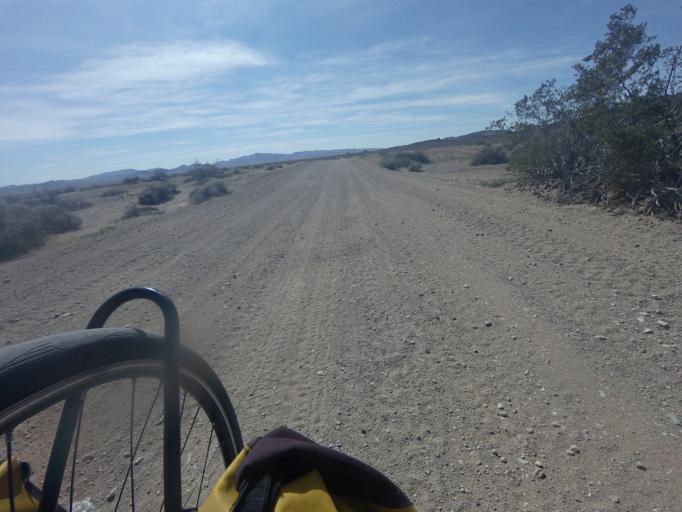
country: US
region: California
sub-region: San Bernardino County
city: Searles Valley
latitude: 35.5843
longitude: -117.4238
